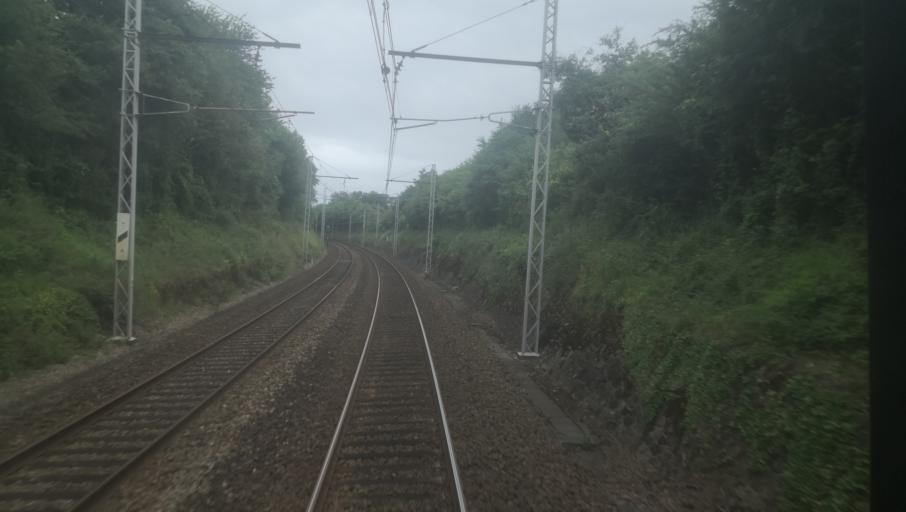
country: FR
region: Centre
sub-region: Departement de l'Indre
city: Le Pechereau
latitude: 46.5502
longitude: 1.5409
